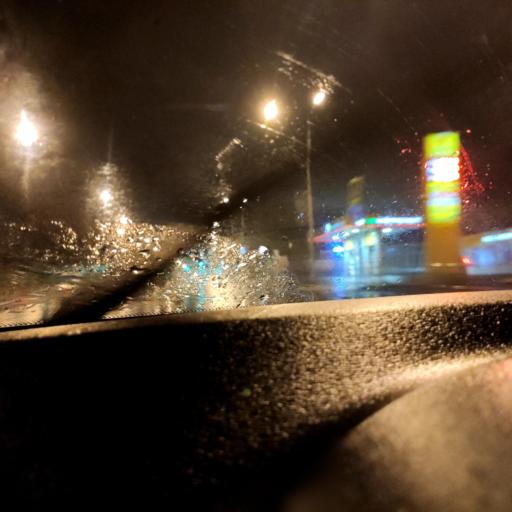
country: RU
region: Samara
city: Petra-Dubrava
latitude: 53.2976
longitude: 50.2442
